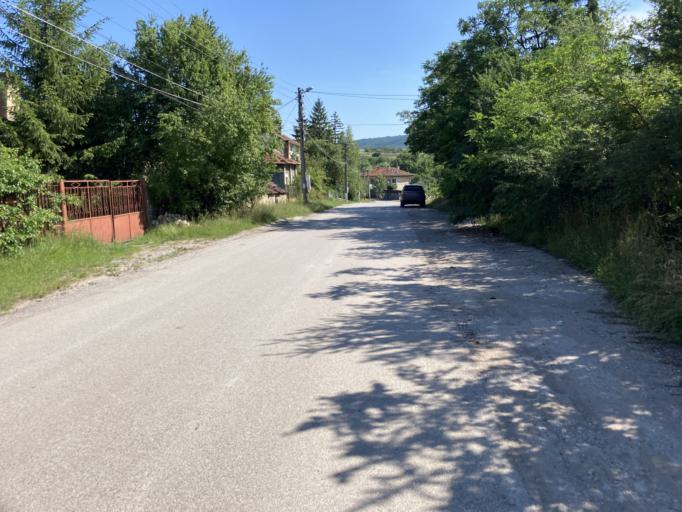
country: BG
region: Sofiya
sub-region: Obshtina Slivnitsa
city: Slivnitsa
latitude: 42.8514
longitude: 22.9813
